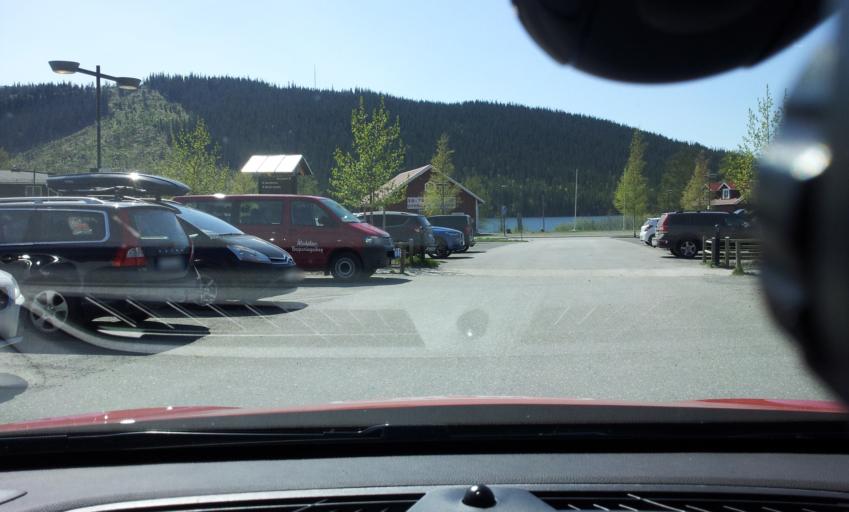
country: SE
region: Jaemtland
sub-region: Are Kommun
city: Are
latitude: 63.3975
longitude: 13.0774
